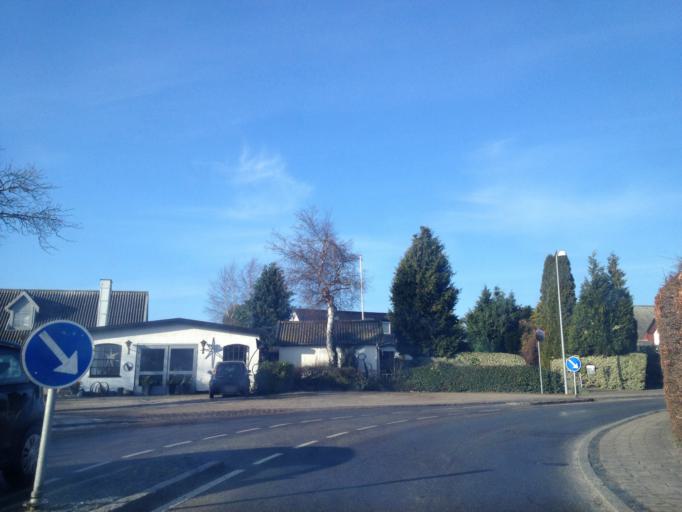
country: DK
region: Zealand
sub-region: Greve Kommune
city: Greve
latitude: 55.6082
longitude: 12.2707
